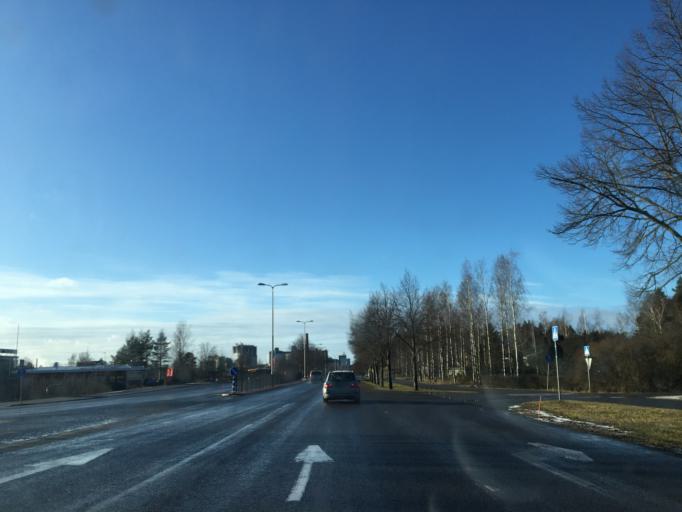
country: FI
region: Varsinais-Suomi
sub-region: Turku
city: Raisio
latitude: 60.4863
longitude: 22.1541
